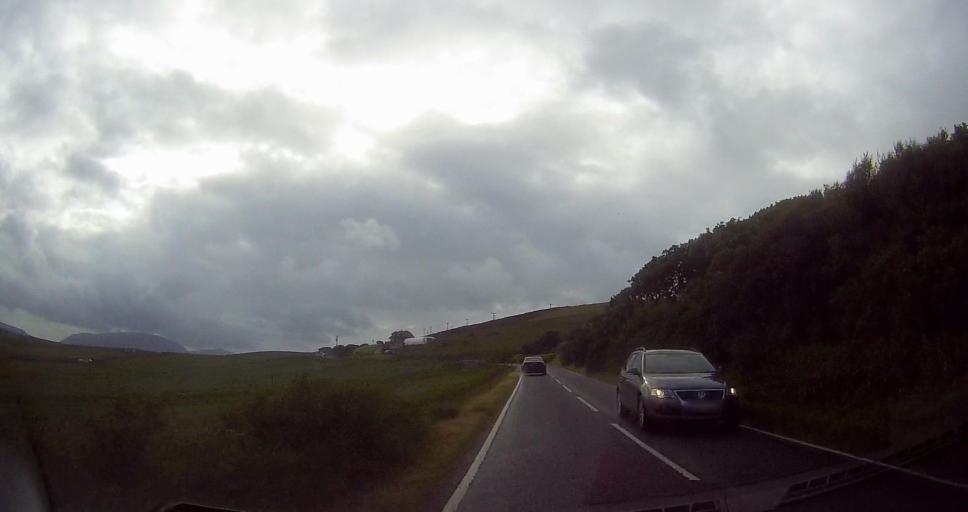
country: GB
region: Scotland
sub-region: Orkney Islands
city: Stromness
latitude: 58.9205
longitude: -3.1845
